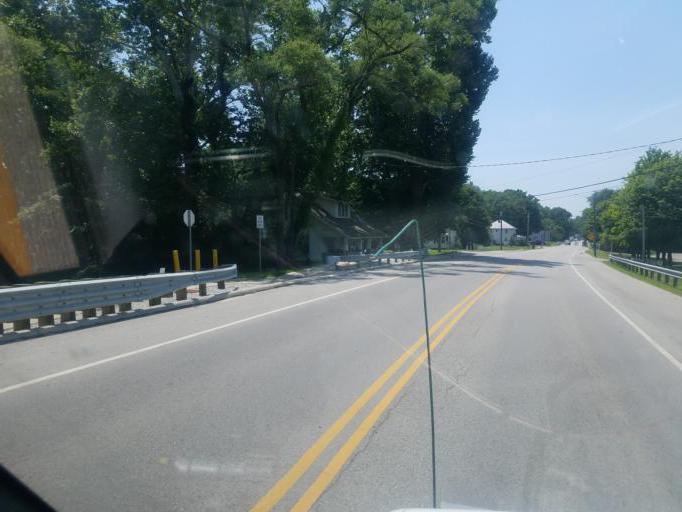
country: US
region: Ohio
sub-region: Shelby County
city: Sidney
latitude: 40.2908
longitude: -84.1440
